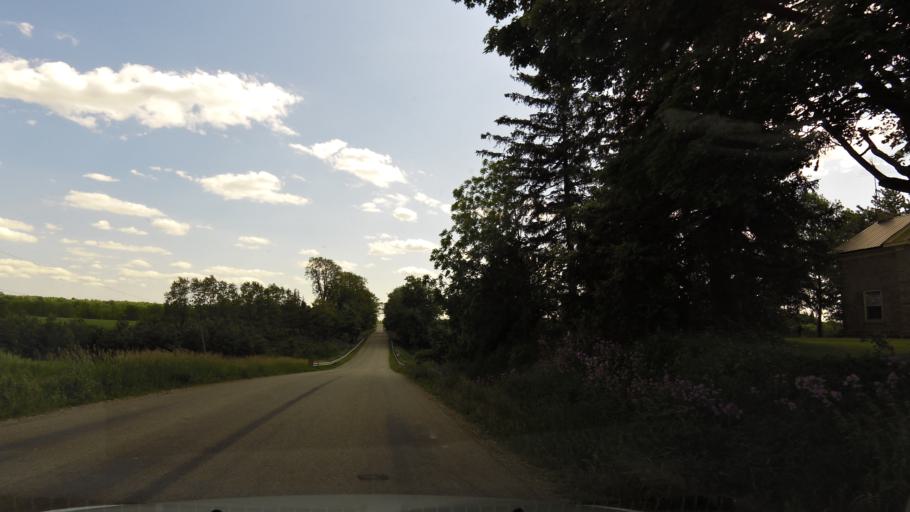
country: CA
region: Ontario
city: Ancaster
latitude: 43.1228
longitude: -80.0840
